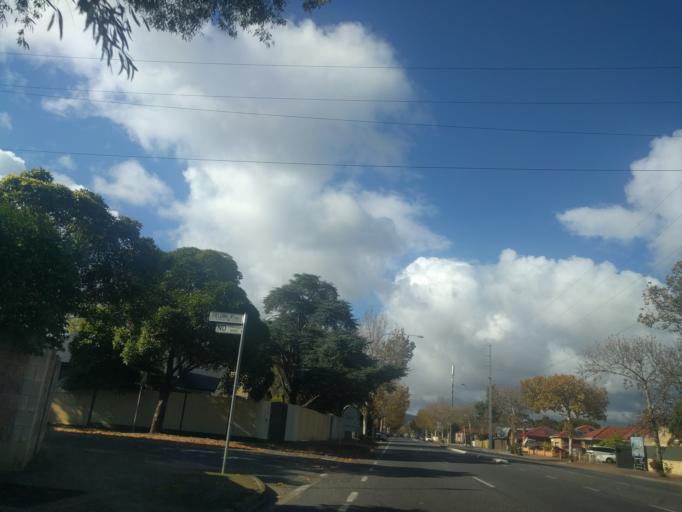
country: AU
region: South Australia
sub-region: Mitcham
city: Clarence Gardens
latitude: -34.9671
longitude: 138.5747
